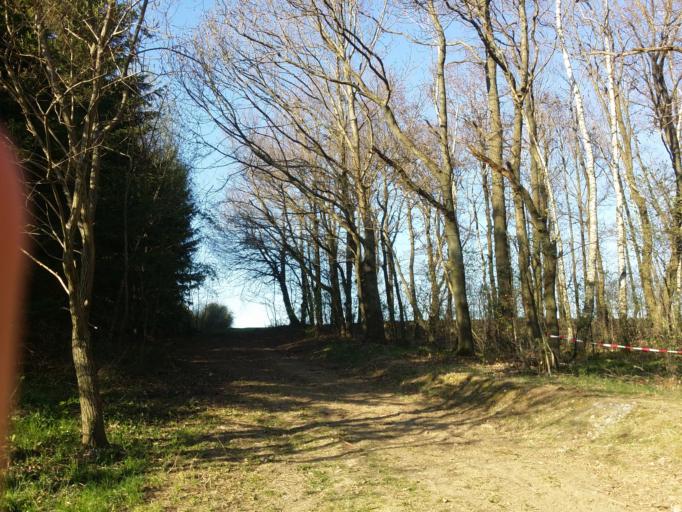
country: DE
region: Saxony
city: Burkhardtsdorf
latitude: 50.7723
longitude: 12.9563
